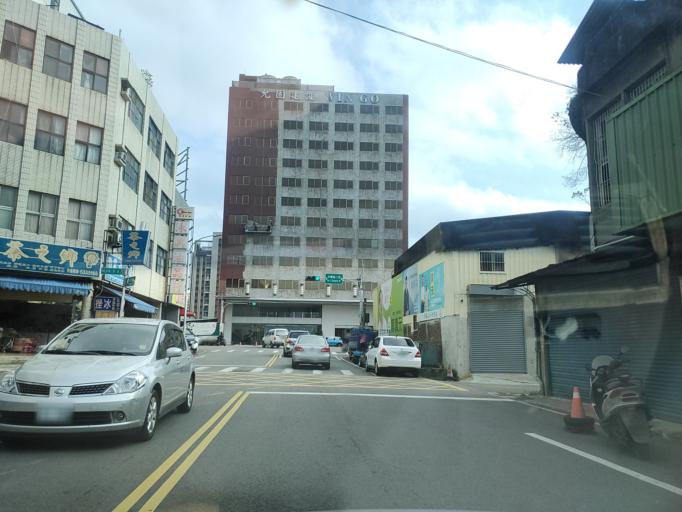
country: TW
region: Taiwan
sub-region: Hsinchu
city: Hsinchu
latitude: 24.8088
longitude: 120.9812
